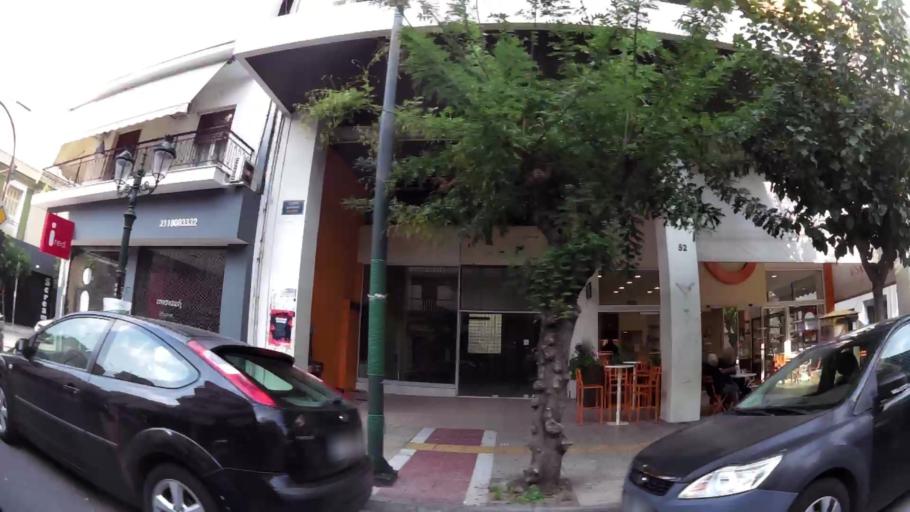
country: GR
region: Attica
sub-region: Nomarchia Athinas
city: Kallithea
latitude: 37.9538
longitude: 23.7043
